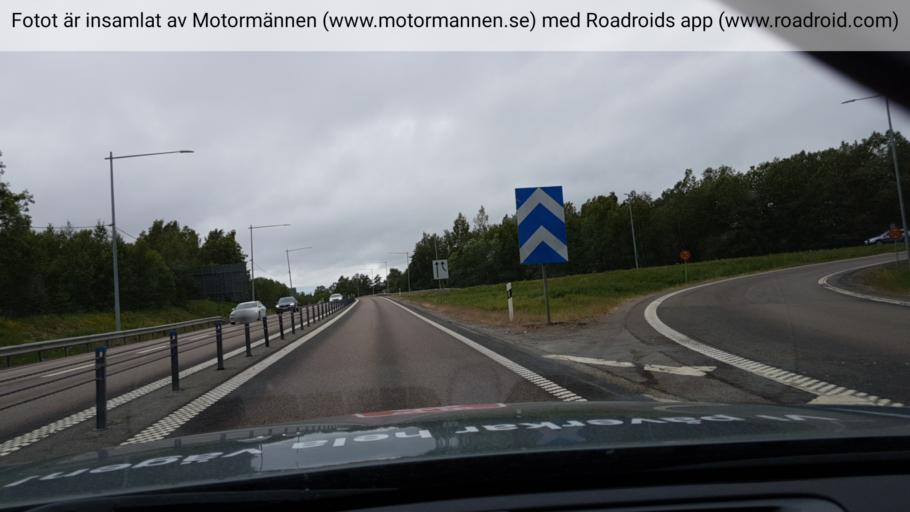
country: SE
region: Vaesternorrland
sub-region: Timra Kommun
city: Bergeforsen
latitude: 62.5168
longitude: 17.3914
